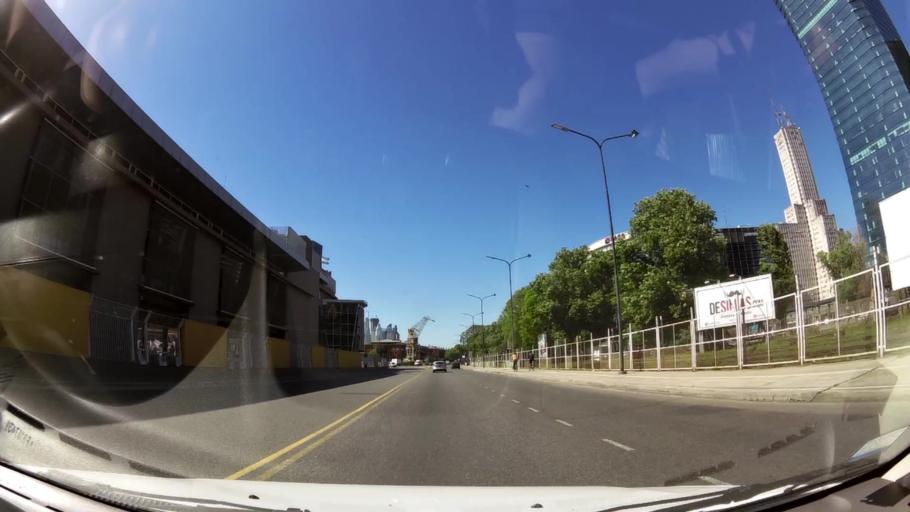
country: AR
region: Buenos Aires F.D.
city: Buenos Aires
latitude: -34.5969
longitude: -58.3686
